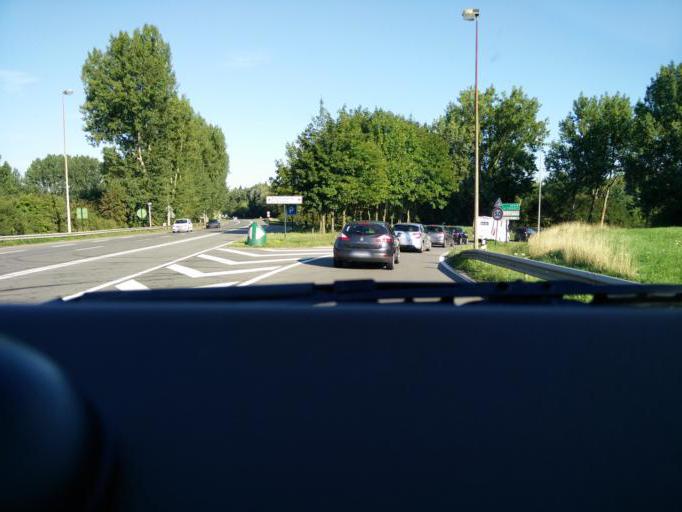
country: FR
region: Nord-Pas-de-Calais
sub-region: Departement du Pas-de-Calais
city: Divion
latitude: 50.4726
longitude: 2.5221
